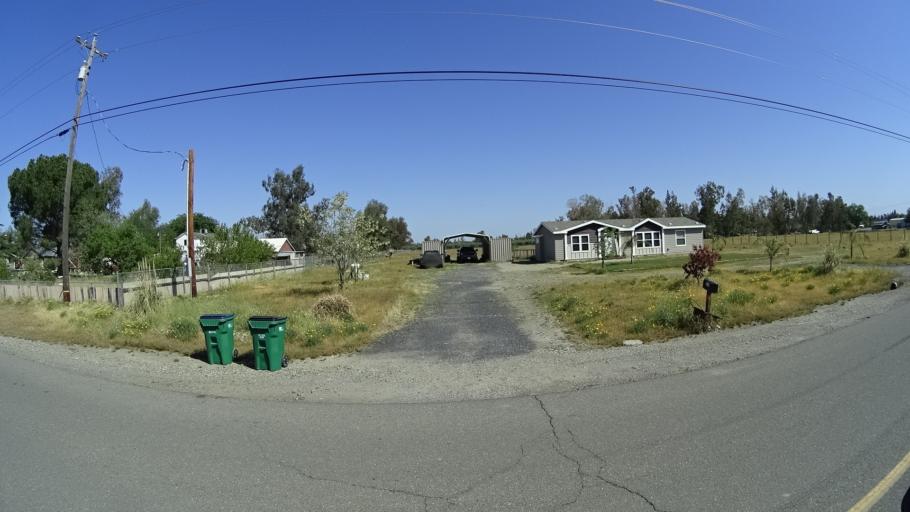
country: US
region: California
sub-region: Glenn County
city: Orland
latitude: 39.7254
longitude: -122.1711
